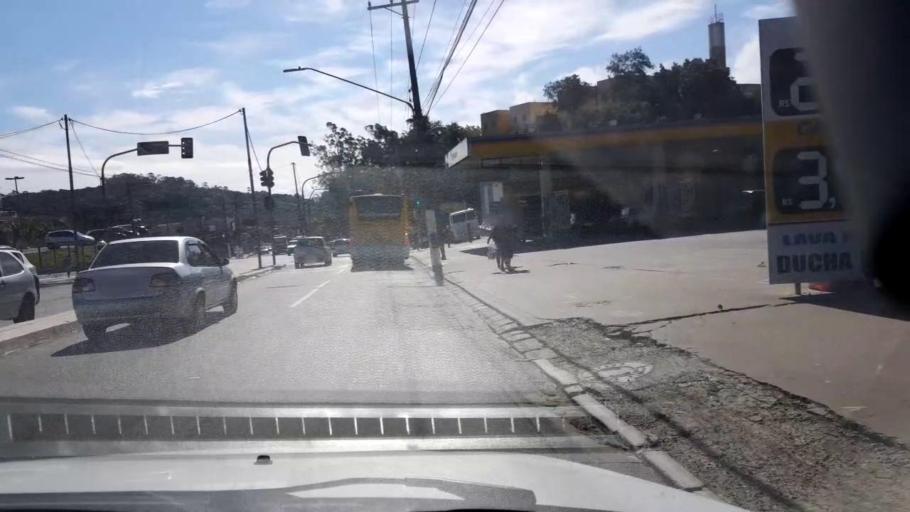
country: BR
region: Sao Paulo
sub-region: Ferraz De Vasconcelos
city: Ferraz de Vasconcelos
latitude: -23.5831
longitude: -46.4150
